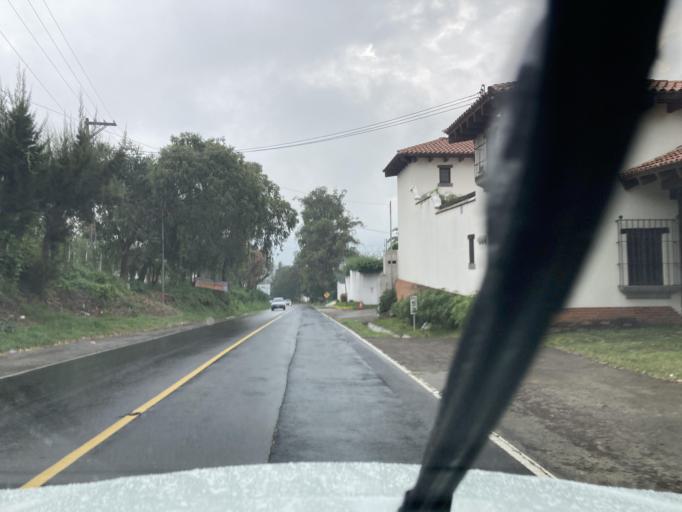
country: GT
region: Sacatepequez
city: San Miguel Duenas
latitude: 14.5189
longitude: -90.7821
